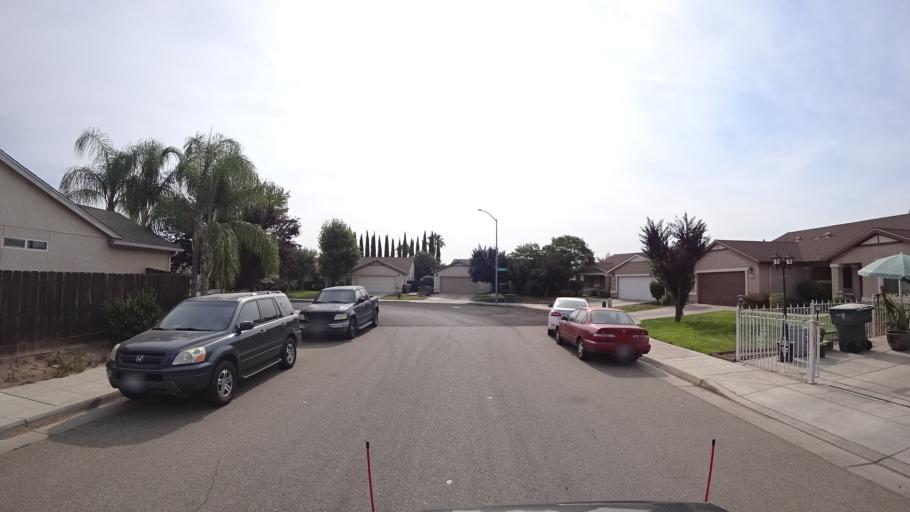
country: US
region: California
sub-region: Fresno County
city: West Park
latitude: 36.7686
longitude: -119.8667
